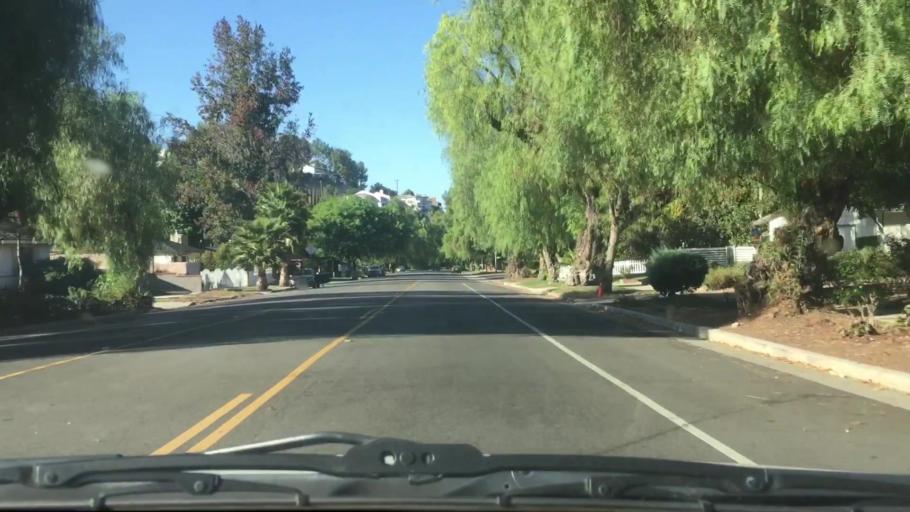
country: US
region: California
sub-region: Los Angeles County
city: Woodland Hills
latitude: 34.1609
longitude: -118.5964
